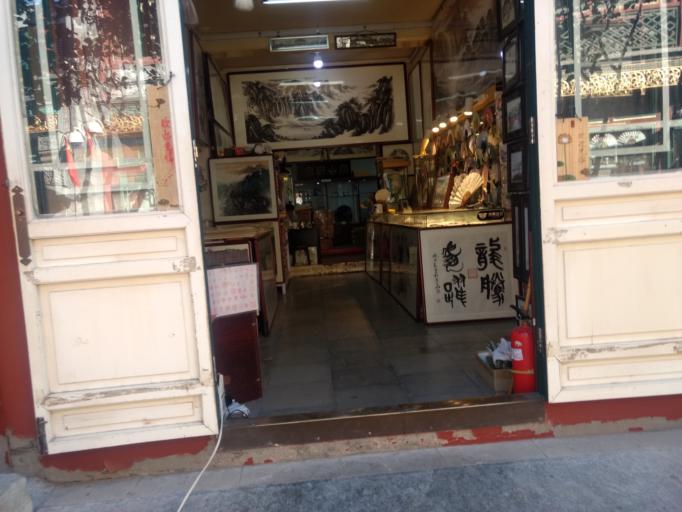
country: CN
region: Beijing
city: Beijing
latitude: 39.8939
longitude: 116.3794
